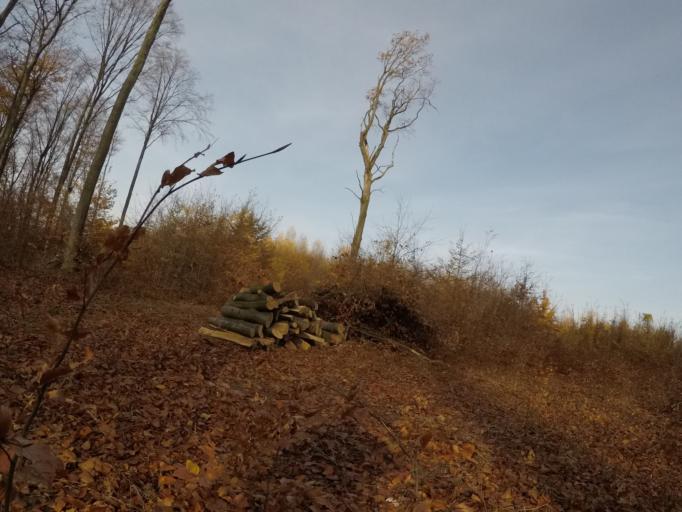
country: SK
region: Presovsky
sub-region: Okres Presov
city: Presov
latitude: 48.9107
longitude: 21.2147
